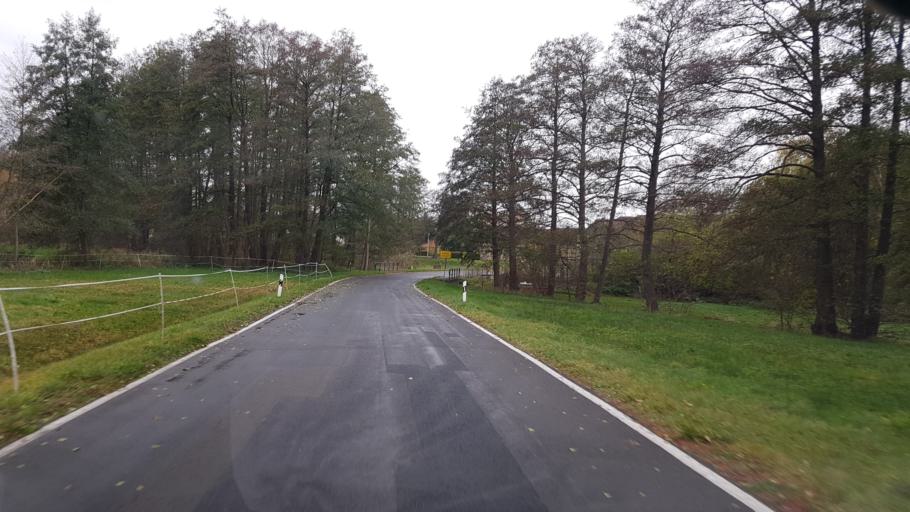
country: DE
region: Brandenburg
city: Ortrand
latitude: 51.3627
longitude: 13.7614
